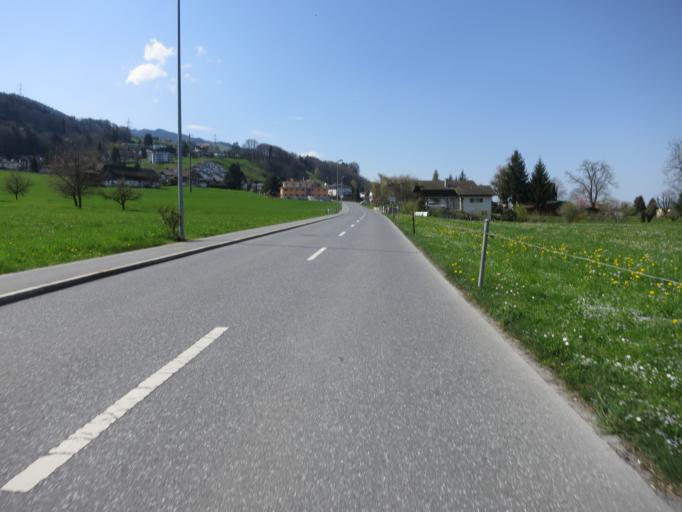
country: CH
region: Schwyz
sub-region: Bezirk March
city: Lachen
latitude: 47.1742
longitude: 8.8846
